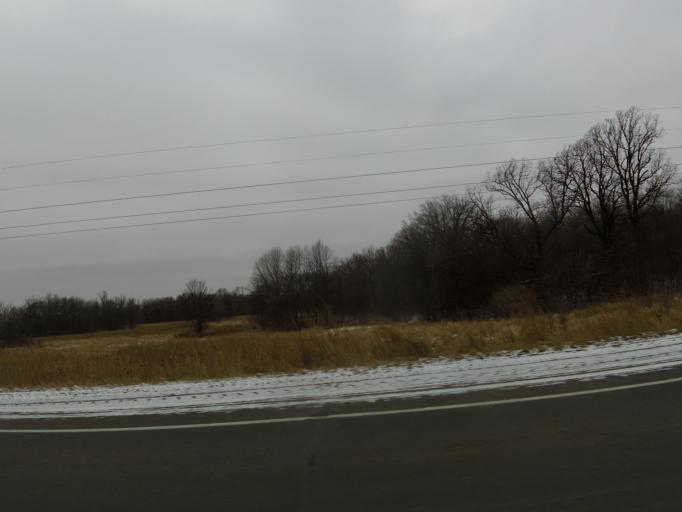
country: US
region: Minnesota
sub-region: Wright County
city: Delano
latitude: 45.0556
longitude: -93.8035
